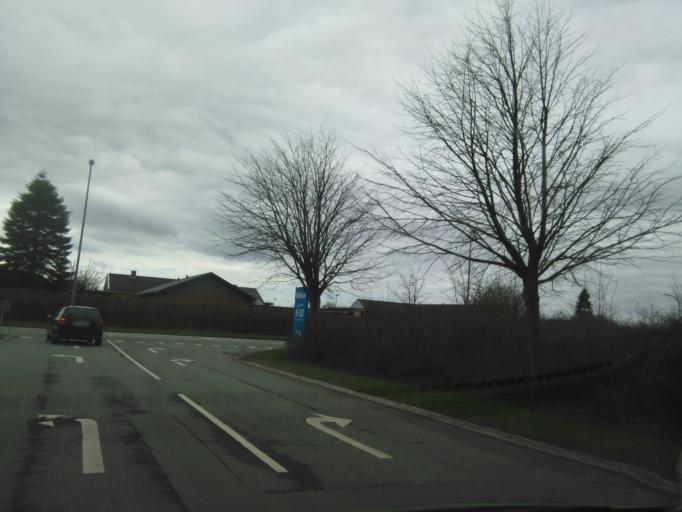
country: DK
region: Central Jutland
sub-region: Arhus Kommune
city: Stavtrup
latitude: 56.1818
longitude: 10.1088
